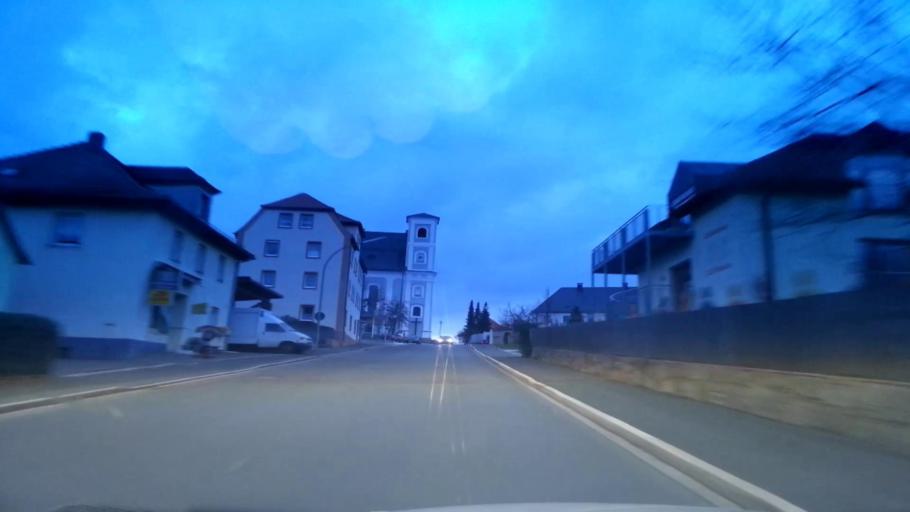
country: DE
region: Bavaria
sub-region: Upper Palatinate
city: Fuchsmuhl
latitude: 49.9253
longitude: 12.1438
